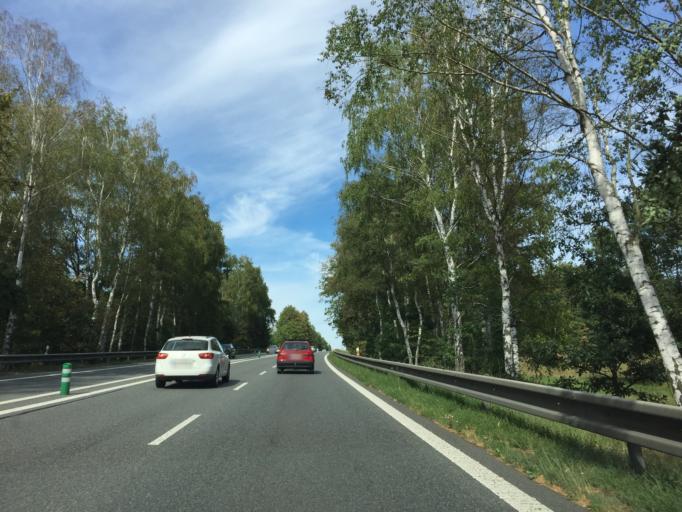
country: CZ
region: Central Bohemia
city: Porici nad Sazavou
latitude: 49.8515
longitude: 14.6838
